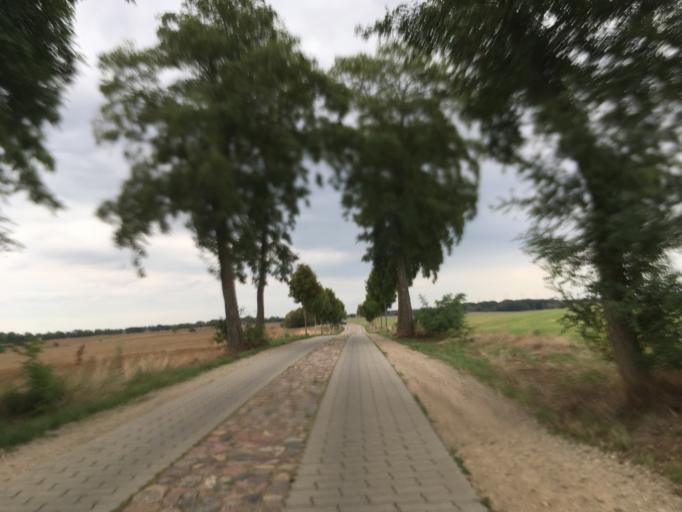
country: DE
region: Brandenburg
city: Pinnow
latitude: 53.0811
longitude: 14.1060
